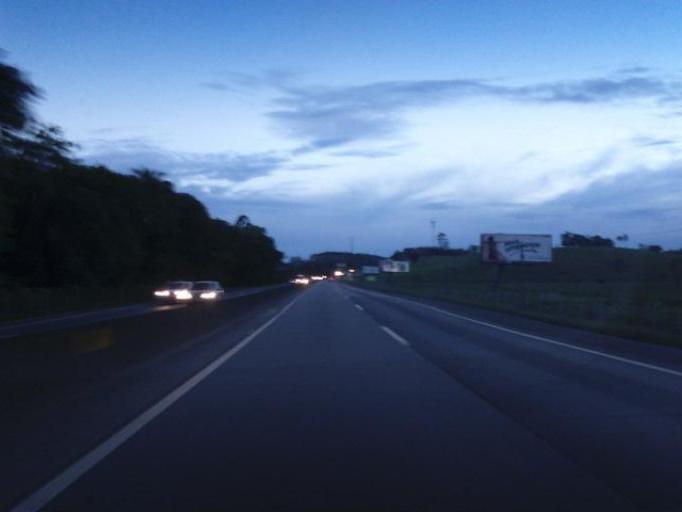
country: BR
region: Santa Catarina
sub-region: Joinville
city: Joinville
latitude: -26.4056
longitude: -48.8384
